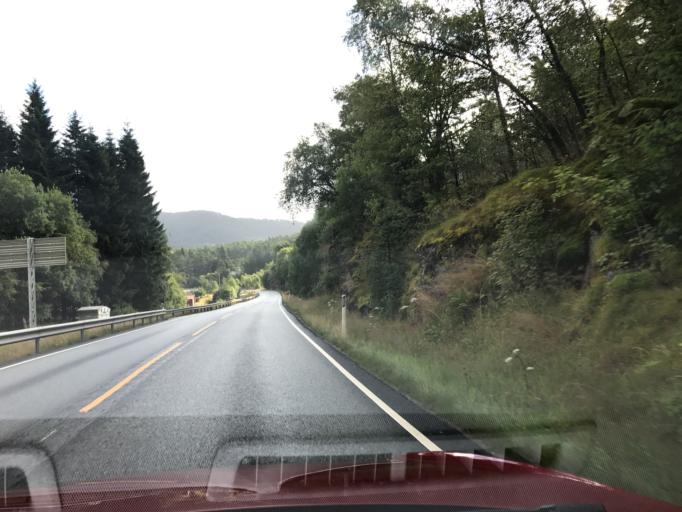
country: NO
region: Hordaland
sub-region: Sveio
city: Sveio
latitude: 59.5825
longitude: 5.4373
